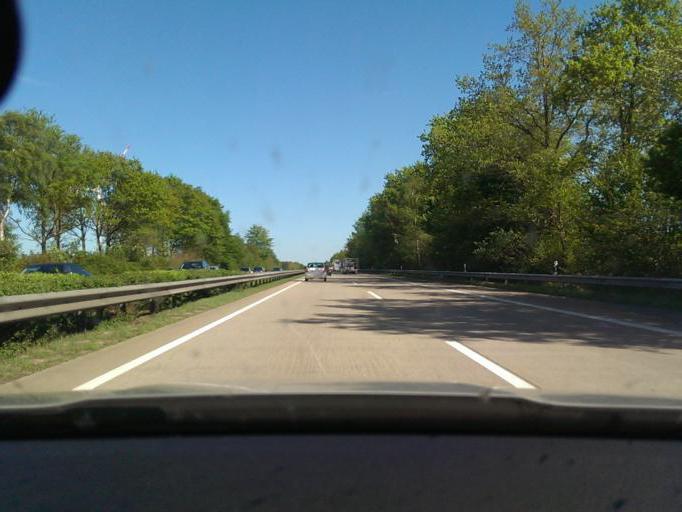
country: DE
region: Lower Saxony
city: Hauslingen
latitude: 52.8853
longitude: 9.4593
